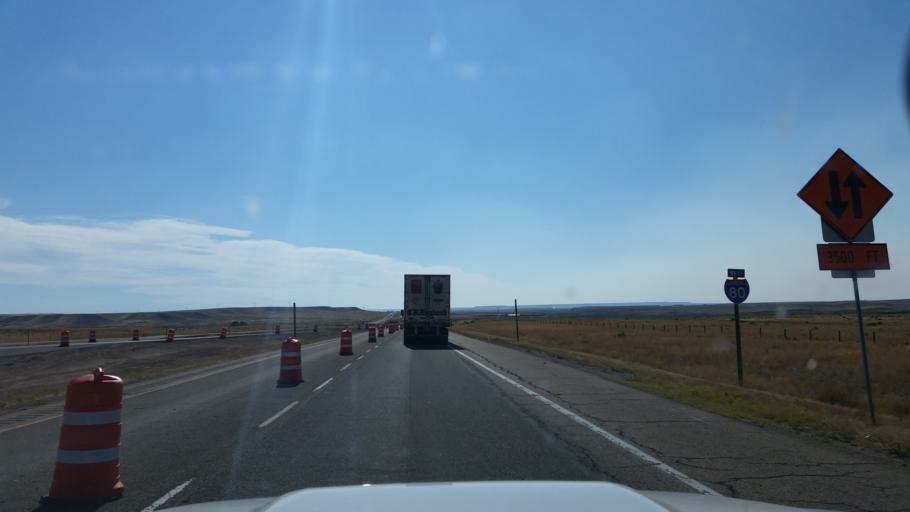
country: US
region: Wyoming
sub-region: Uinta County
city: Lyman
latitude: 41.3908
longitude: -110.1931
